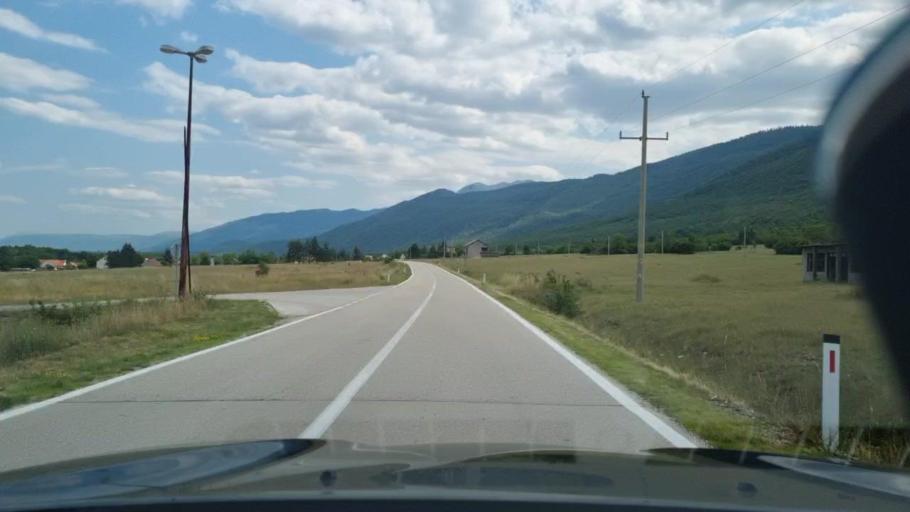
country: BA
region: Federation of Bosnia and Herzegovina
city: Glamoc
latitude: 44.0319
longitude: 16.5959
